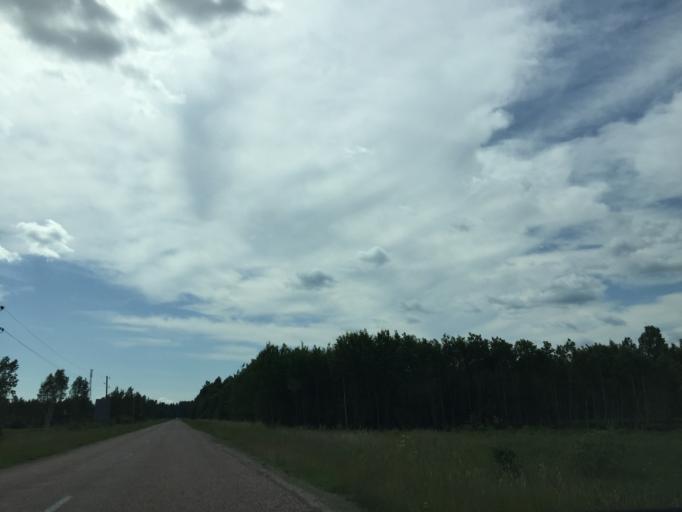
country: LV
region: Engure
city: Smarde
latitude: 57.0581
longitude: 23.2998
